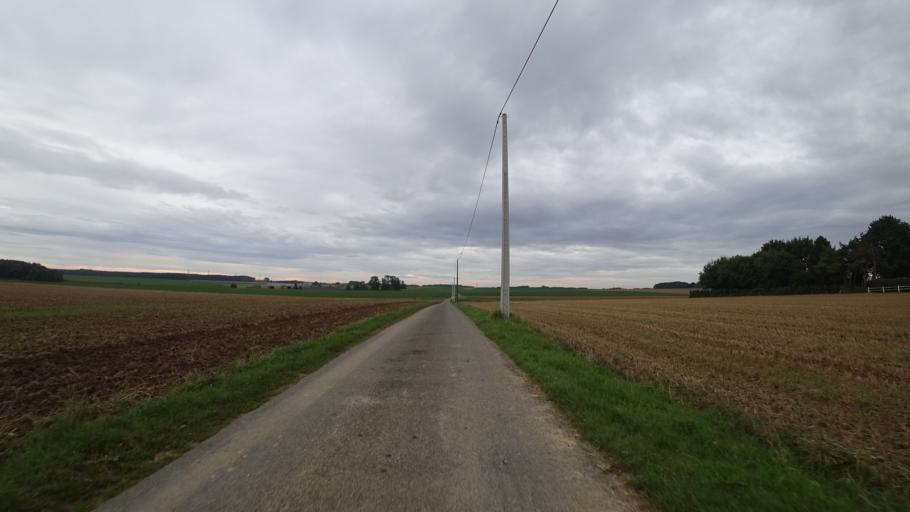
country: BE
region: Wallonia
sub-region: Province du Brabant Wallon
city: Perwez
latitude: 50.5499
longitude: 4.8117
